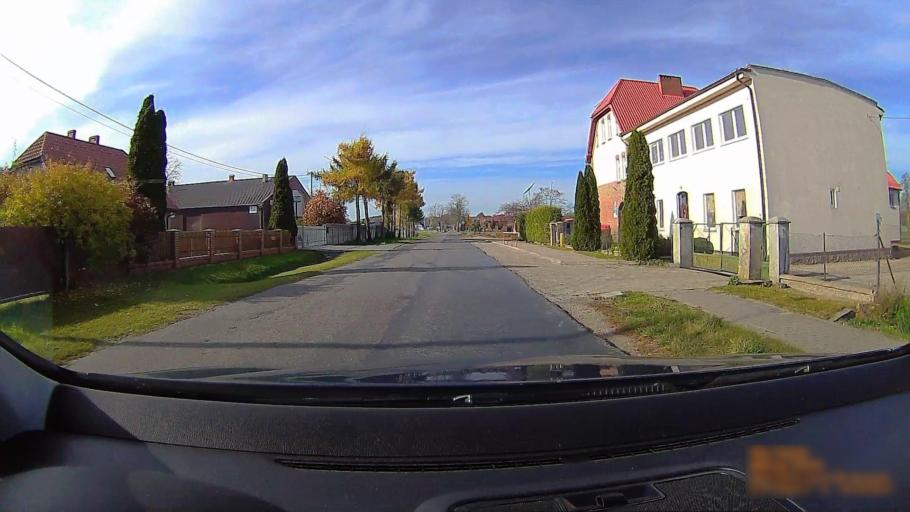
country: PL
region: Greater Poland Voivodeship
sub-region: Powiat ostrzeszowski
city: Doruchow
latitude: 51.4295
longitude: 18.0384
